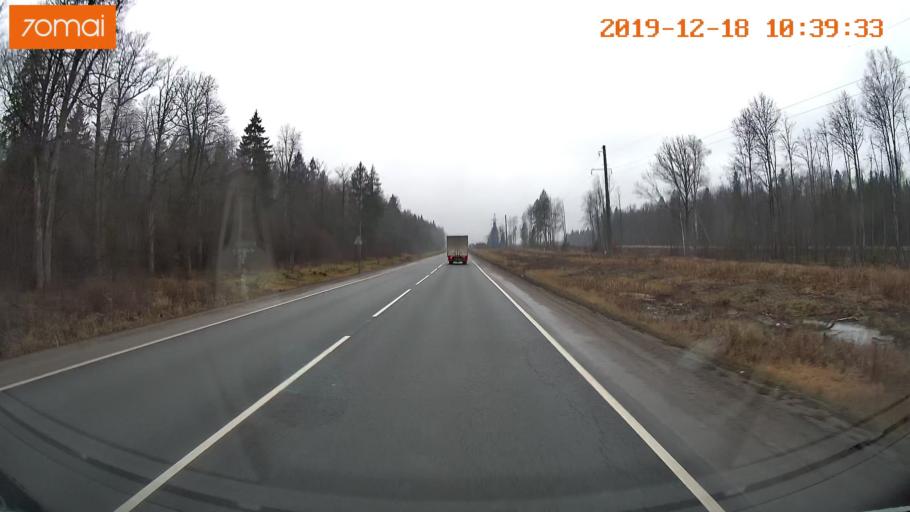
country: RU
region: Moskovskaya
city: Aprelevka
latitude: 55.4442
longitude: 37.1388
